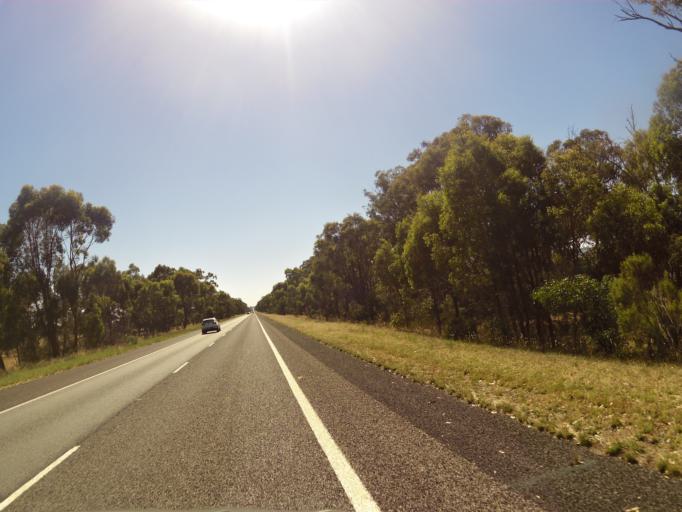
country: AU
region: Victoria
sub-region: Greater Shepparton
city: Shepparton
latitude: -36.8595
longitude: 145.3110
